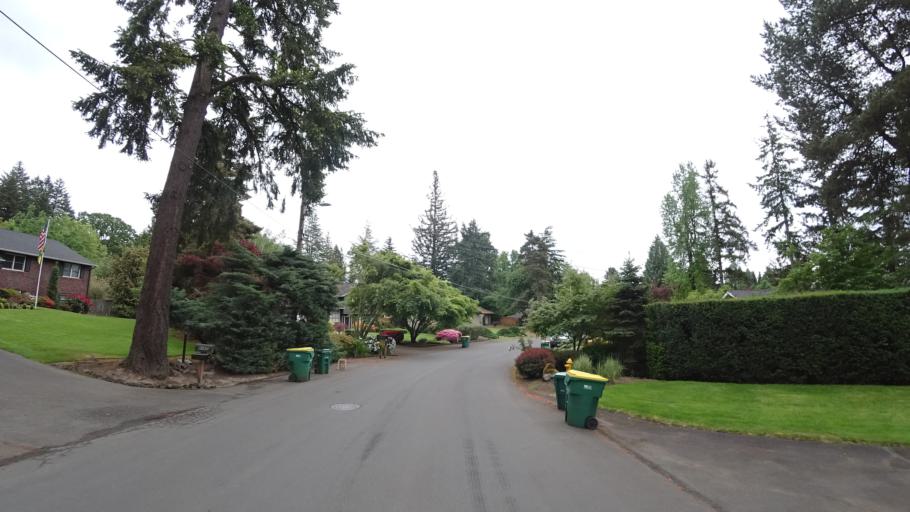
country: US
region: Oregon
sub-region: Washington County
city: Raleigh Hills
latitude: 45.4828
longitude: -122.7629
